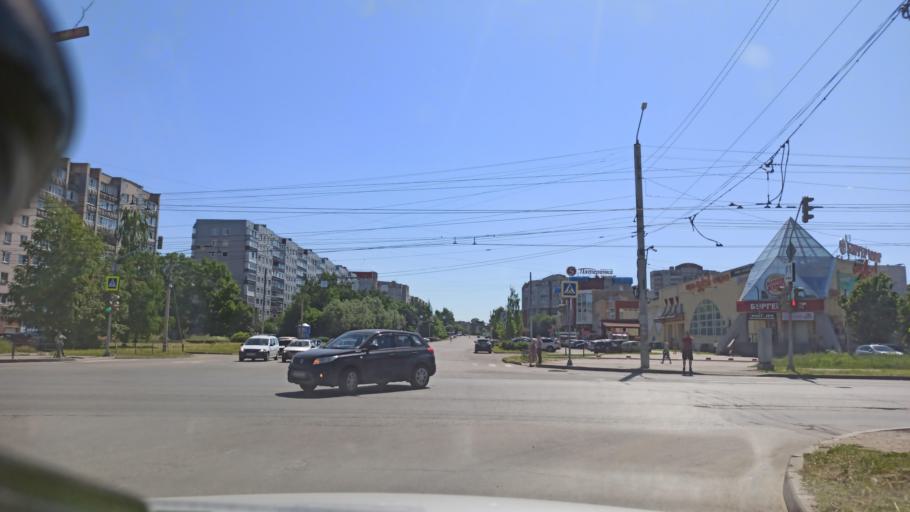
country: RU
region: Vologda
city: Vologda
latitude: 59.2060
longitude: 39.8381
